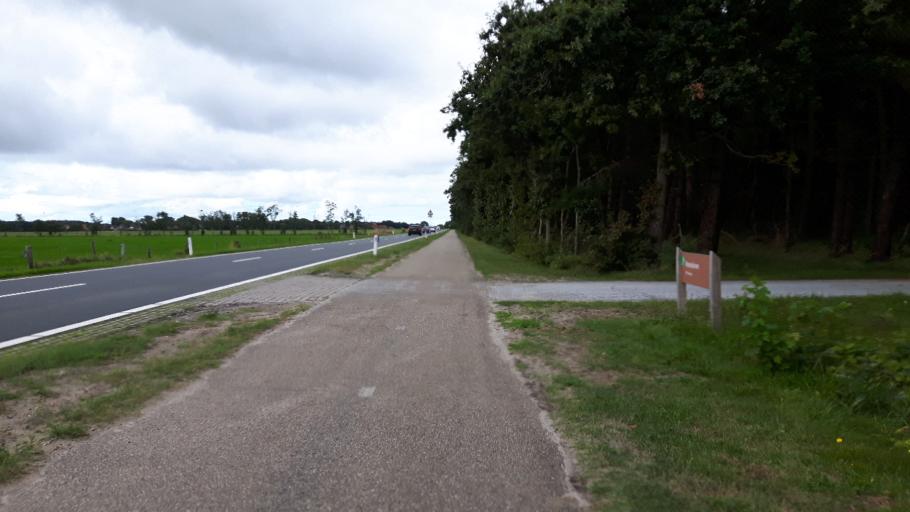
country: NL
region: Friesland
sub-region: Gemeente Ameland
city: Hollum
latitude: 53.4464
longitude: 5.7047
